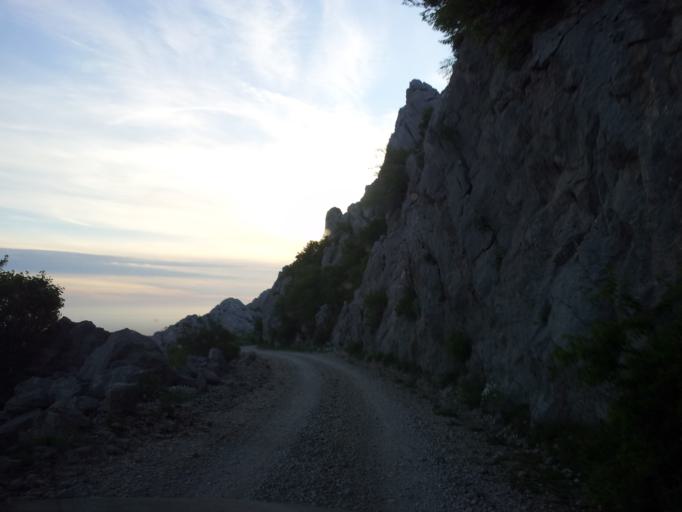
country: HR
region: Zadarska
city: Obrovac
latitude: 44.2612
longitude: 15.6483
